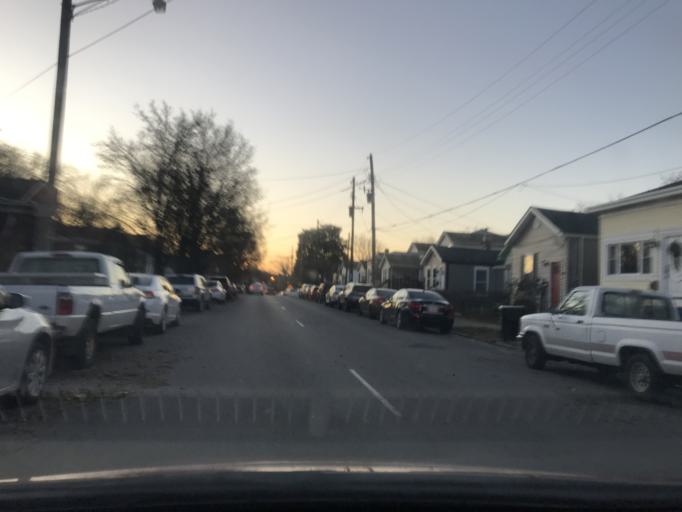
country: US
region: Kentucky
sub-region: Jefferson County
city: Audubon Park
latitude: 38.2337
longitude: -85.7348
